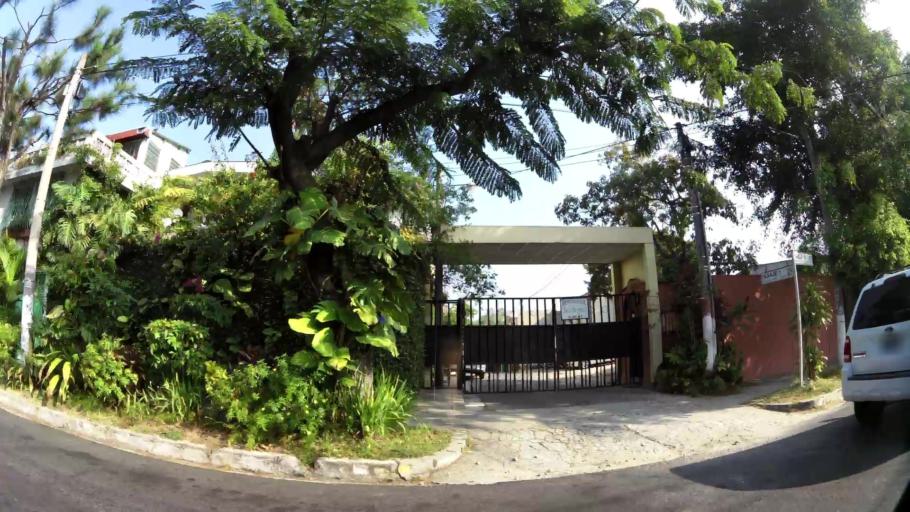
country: SV
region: La Libertad
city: Antiguo Cuscatlan
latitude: 13.6682
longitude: -89.2254
